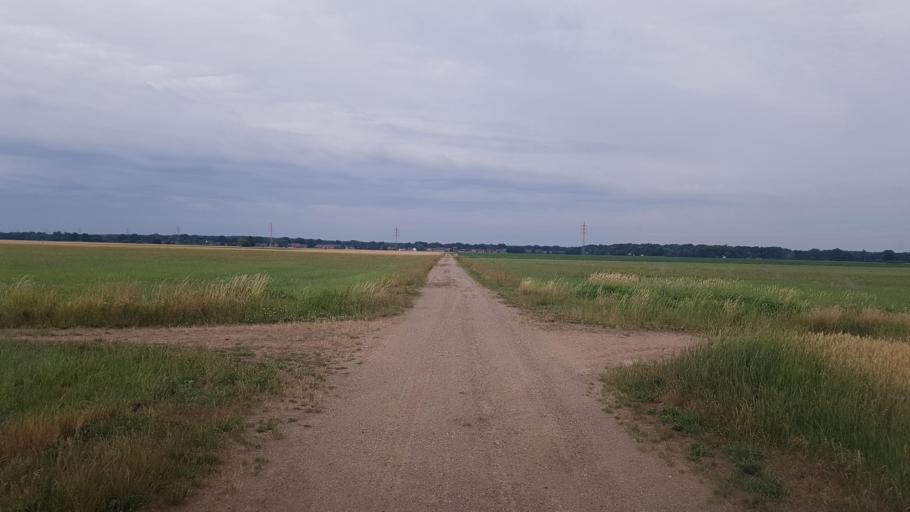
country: DE
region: Saxony-Anhalt
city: Holzdorf
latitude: 51.7517
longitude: 13.1809
